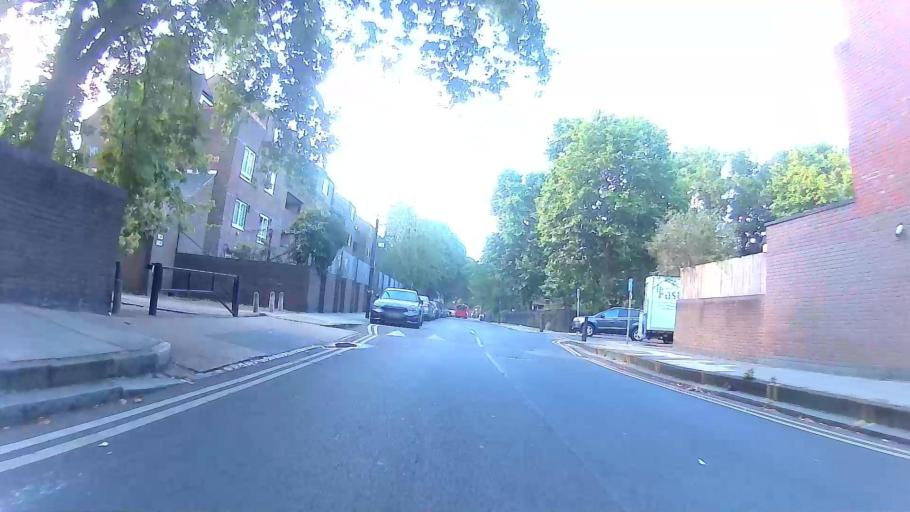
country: GB
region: England
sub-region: Greater London
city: Poplar
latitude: 51.5240
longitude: -0.0192
